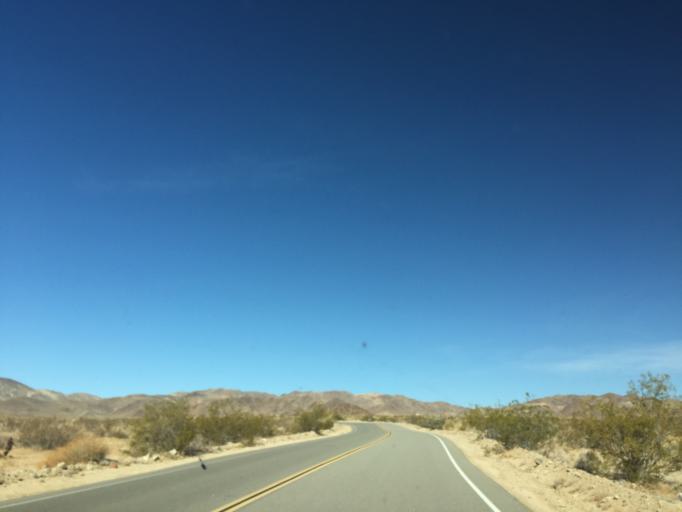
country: US
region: California
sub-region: San Bernardino County
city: Twentynine Palms
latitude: 33.9237
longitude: -115.9222
